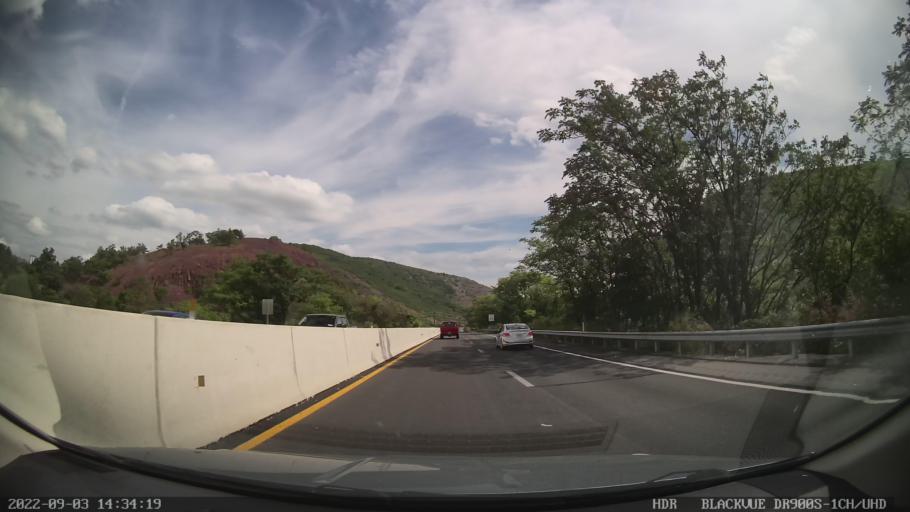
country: US
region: Pennsylvania
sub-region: Carbon County
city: Palmerton
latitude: 40.7956
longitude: -75.6188
